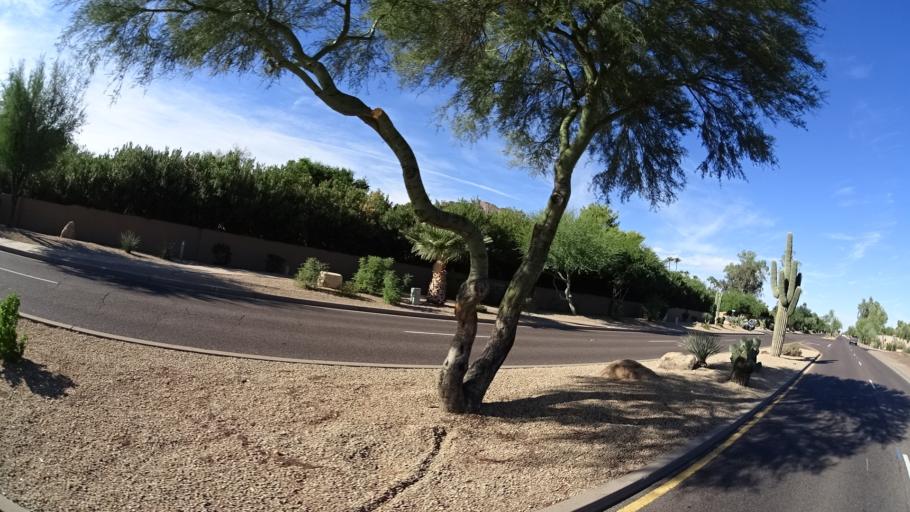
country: US
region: Arizona
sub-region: Maricopa County
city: Paradise Valley
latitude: 33.5311
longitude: -111.9476
